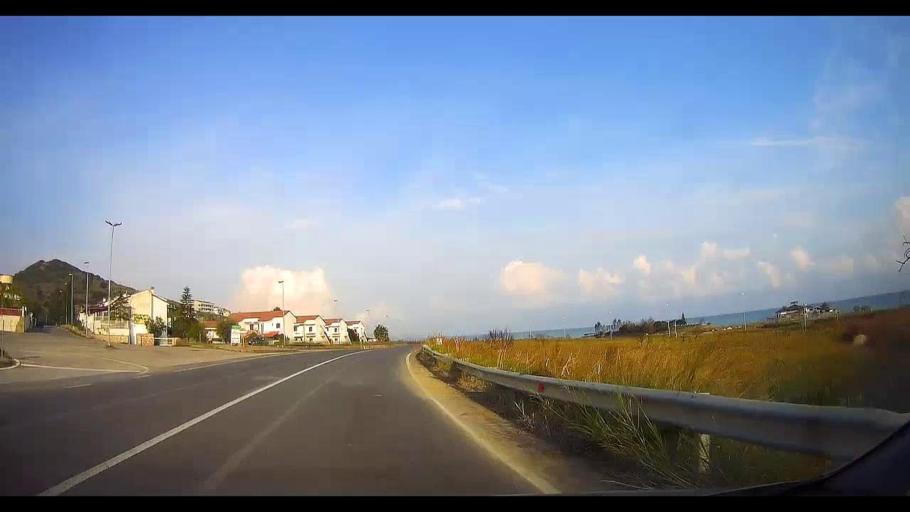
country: IT
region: Calabria
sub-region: Provincia di Cosenza
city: Cariati
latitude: 39.5261
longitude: 16.8894
